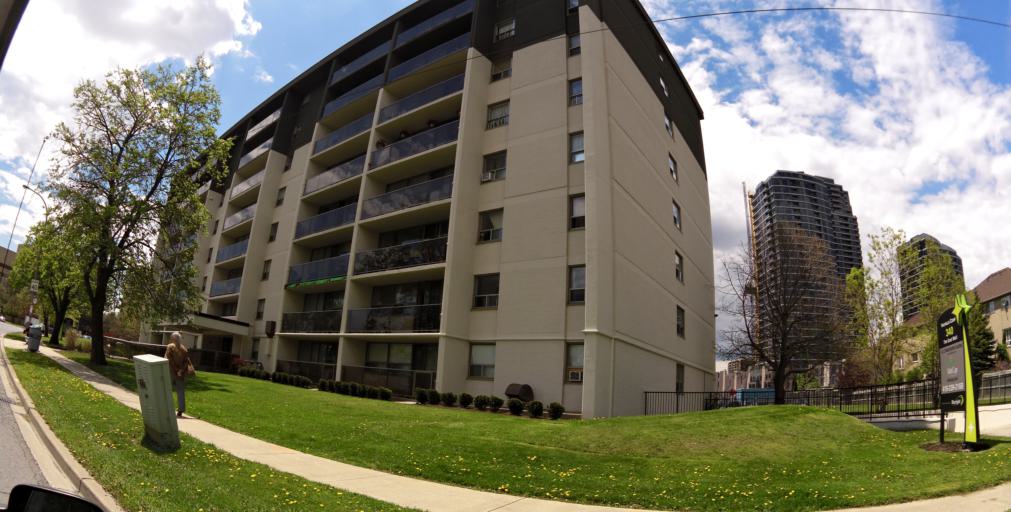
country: CA
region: Ontario
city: Etobicoke
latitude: 43.6394
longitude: -79.5570
